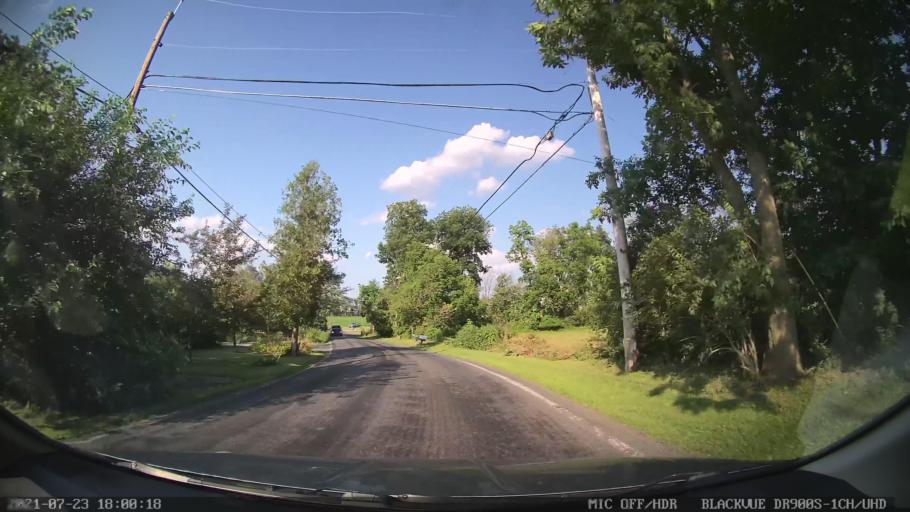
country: US
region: Pennsylvania
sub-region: Lehigh County
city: Macungie
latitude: 40.5239
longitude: -75.5274
